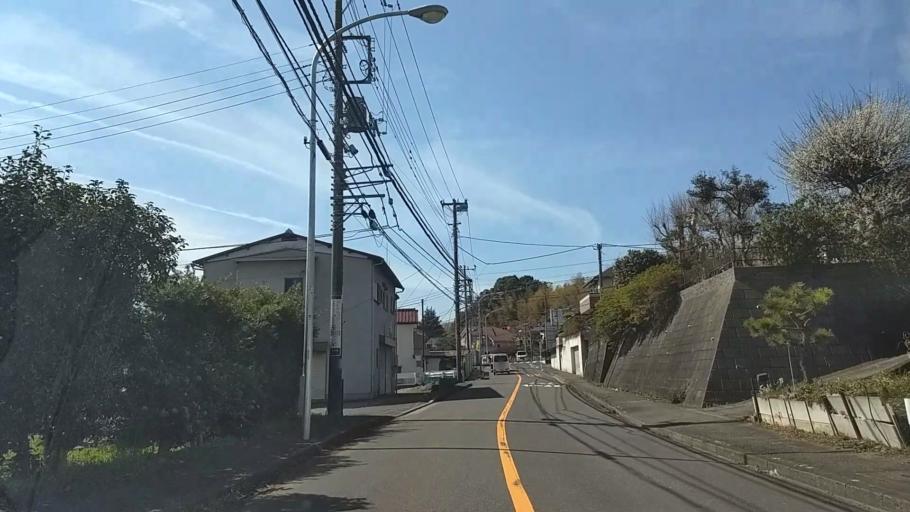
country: JP
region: Kanagawa
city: Fujisawa
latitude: 35.3890
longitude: 139.5081
